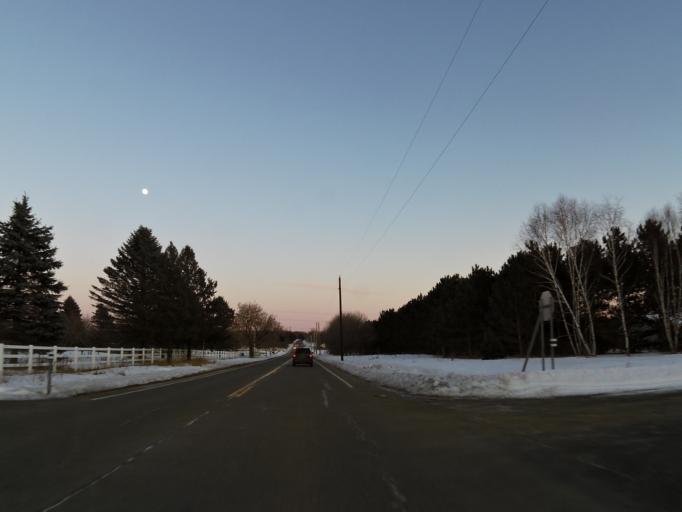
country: US
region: Minnesota
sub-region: Washington County
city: Grant
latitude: 45.0843
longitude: -92.9206
